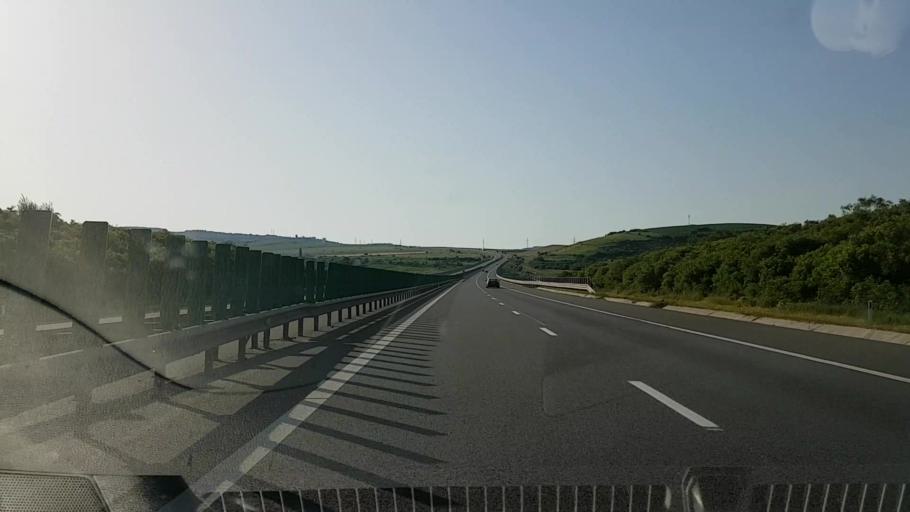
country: RO
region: Cluj
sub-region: Comuna Sandulesti
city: Copaceni
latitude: 46.5732
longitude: 23.7459
